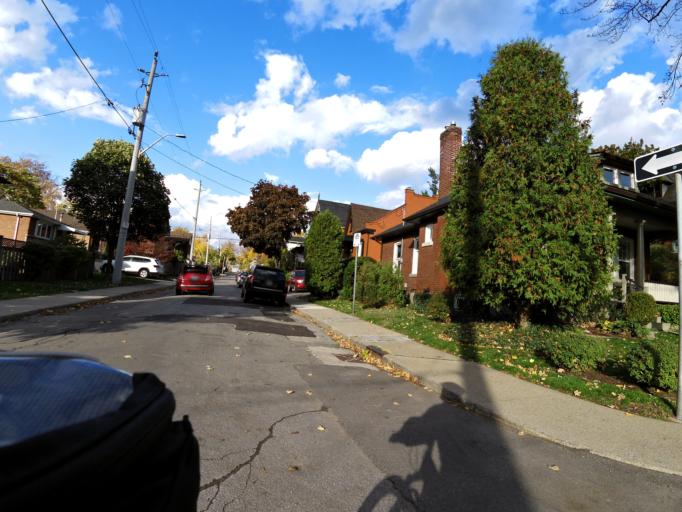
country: CA
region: Ontario
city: Hamilton
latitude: 43.2567
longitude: -79.8817
